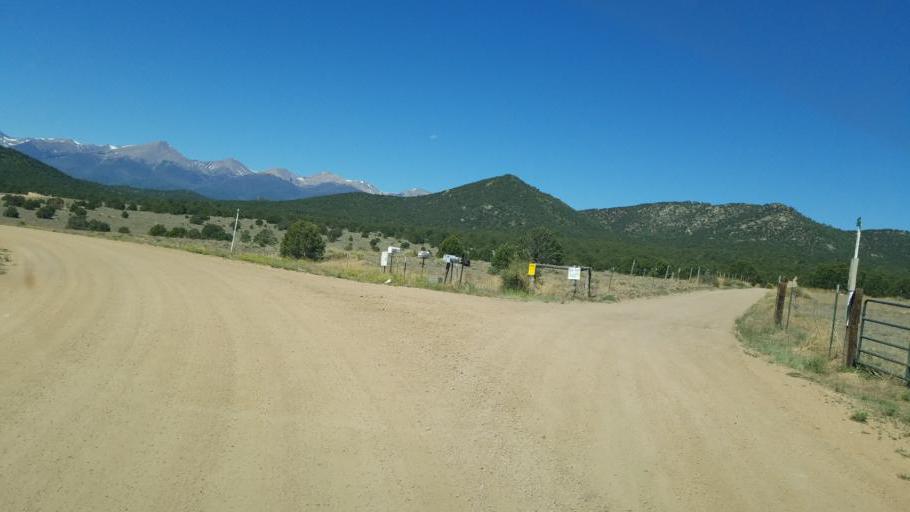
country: US
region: Colorado
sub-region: Custer County
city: Westcliffe
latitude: 38.2852
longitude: -105.5238
